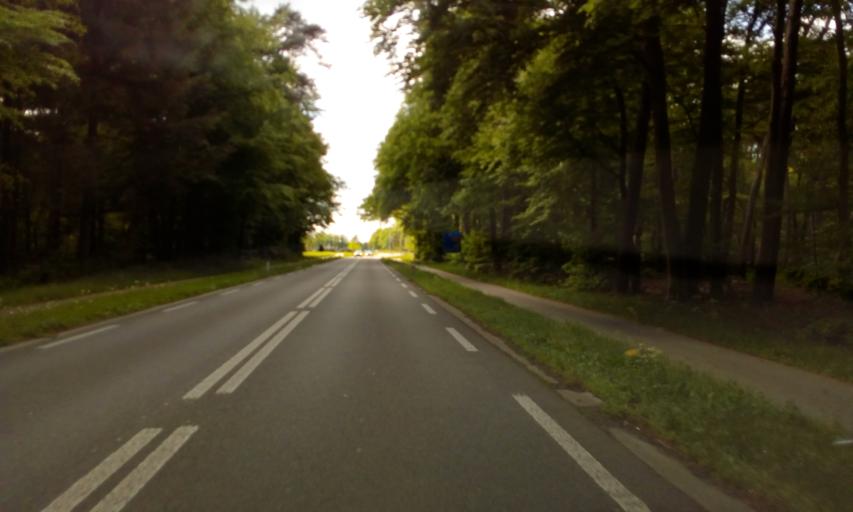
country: NL
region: Gelderland
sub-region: Gemeente Voorst
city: Voorst
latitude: 52.1854
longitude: 6.1126
